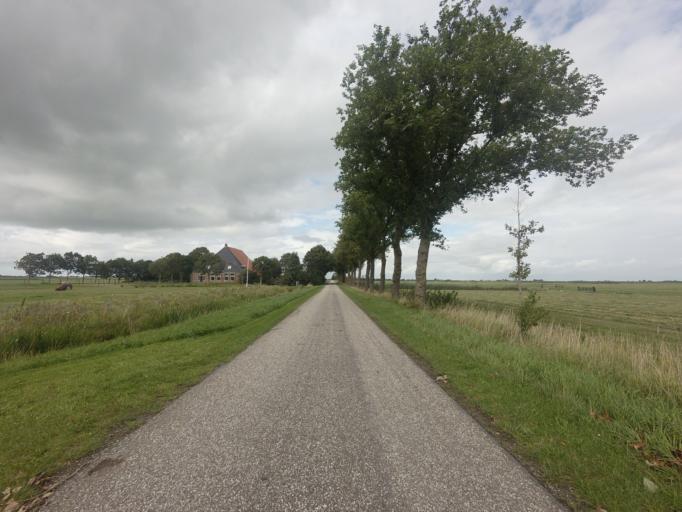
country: NL
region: Friesland
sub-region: Sudwest Fryslan
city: Workum
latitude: 52.9857
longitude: 5.4910
